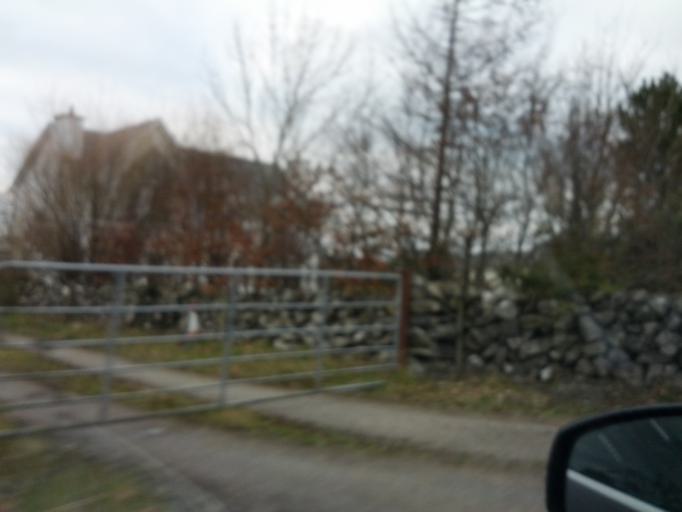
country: IE
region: Connaught
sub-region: County Galway
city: Oranmore
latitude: 53.2241
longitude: -8.8405
